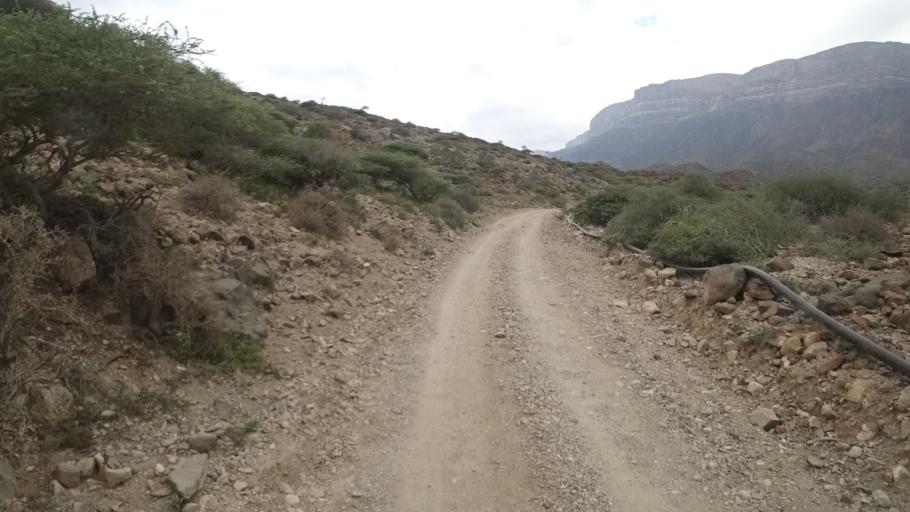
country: OM
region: Zufar
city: Salalah
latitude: 17.1713
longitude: 54.9539
